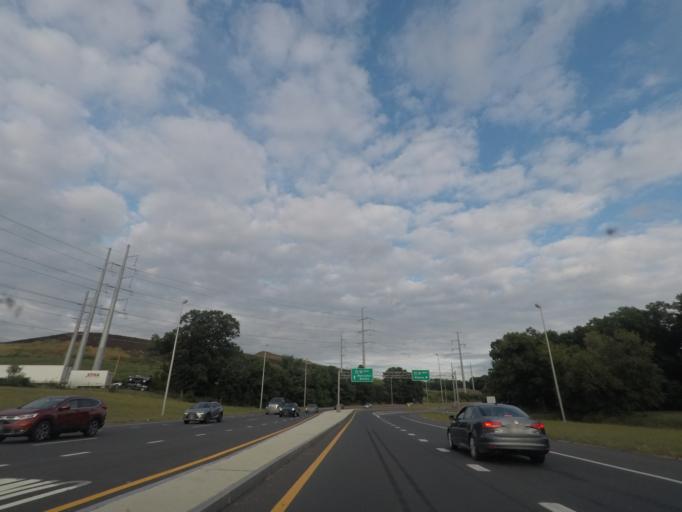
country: US
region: Massachusetts
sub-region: Hampden County
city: North Chicopee
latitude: 42.1637
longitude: -72.5438
